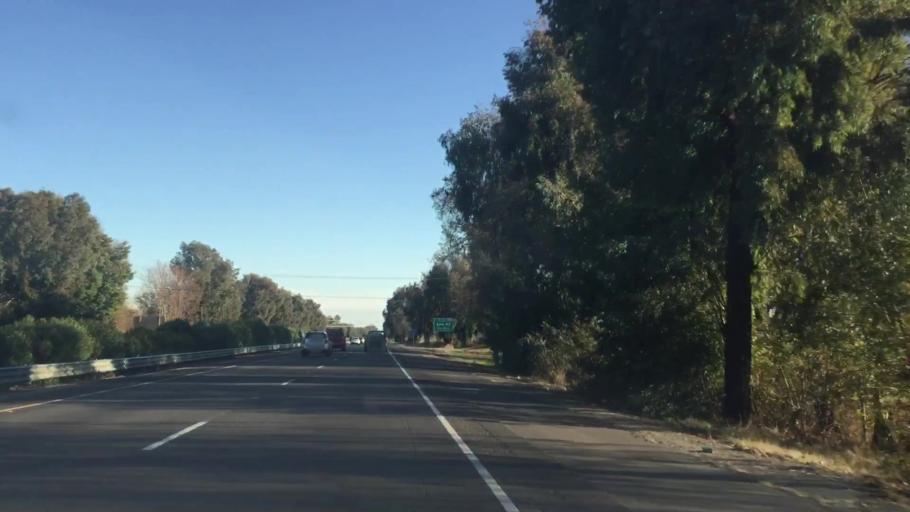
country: US
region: California
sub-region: Yuba County
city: Linda
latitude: 39.1205
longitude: -121.5707
